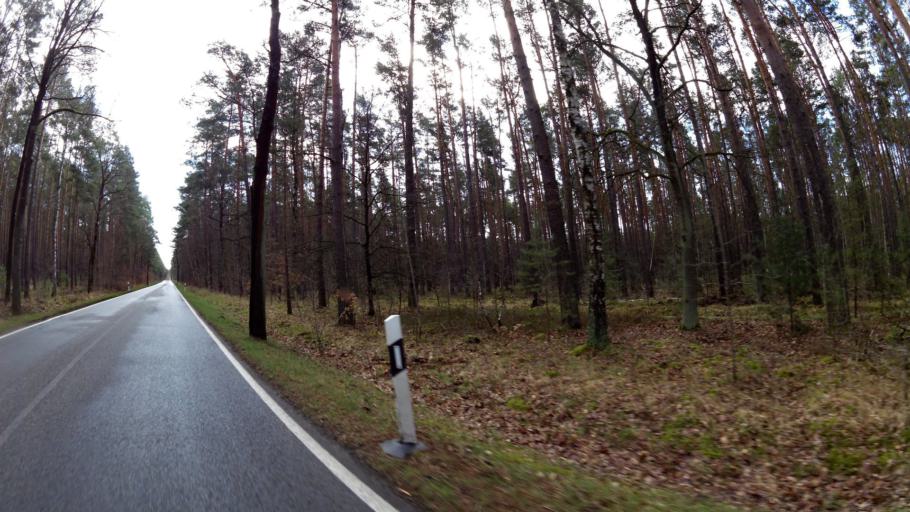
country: DE
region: Brandenburg
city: Bestensee
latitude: 52.2844
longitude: 13.7234
